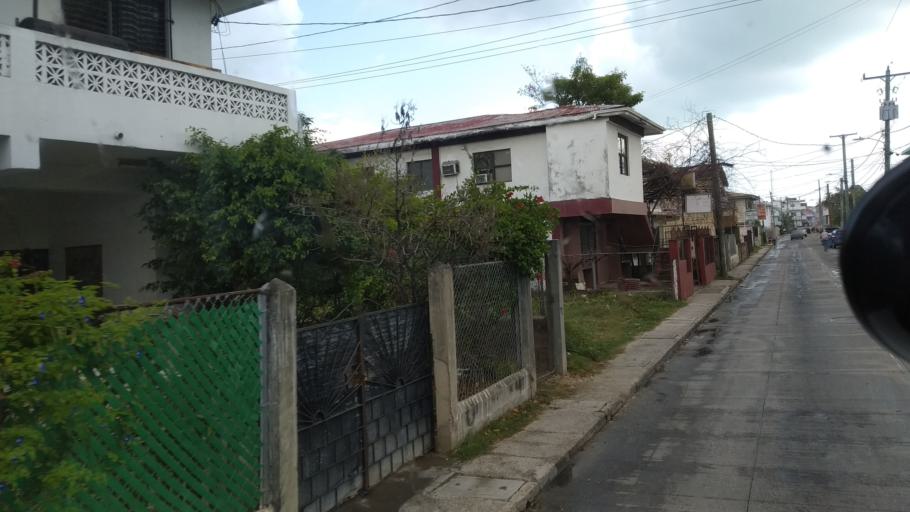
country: BZ
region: Belize
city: Belize City
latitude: 17.4995
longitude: -88.1912
